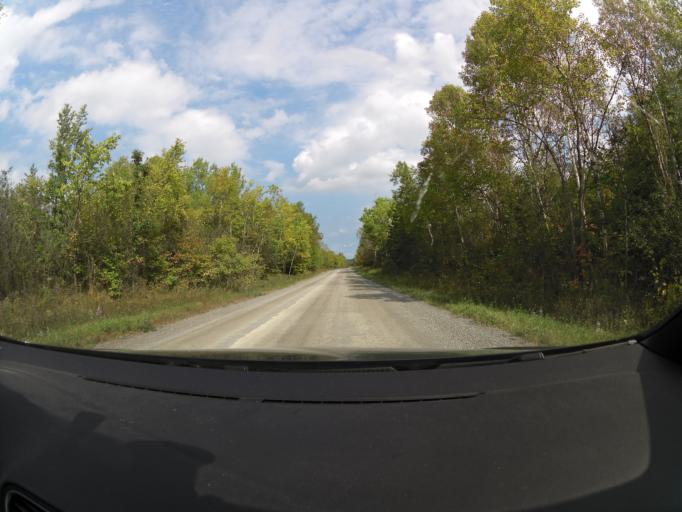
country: CA
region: Ontario
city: Arnprior
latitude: 45.3601
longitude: -76.1804
